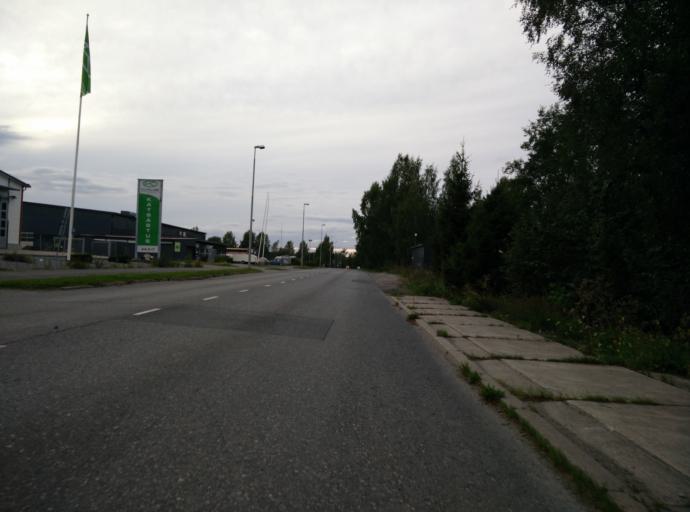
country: FI
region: Haeme
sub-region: Haemeenlinna
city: Haemeenlinna
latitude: 60.9898
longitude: 24.4893
